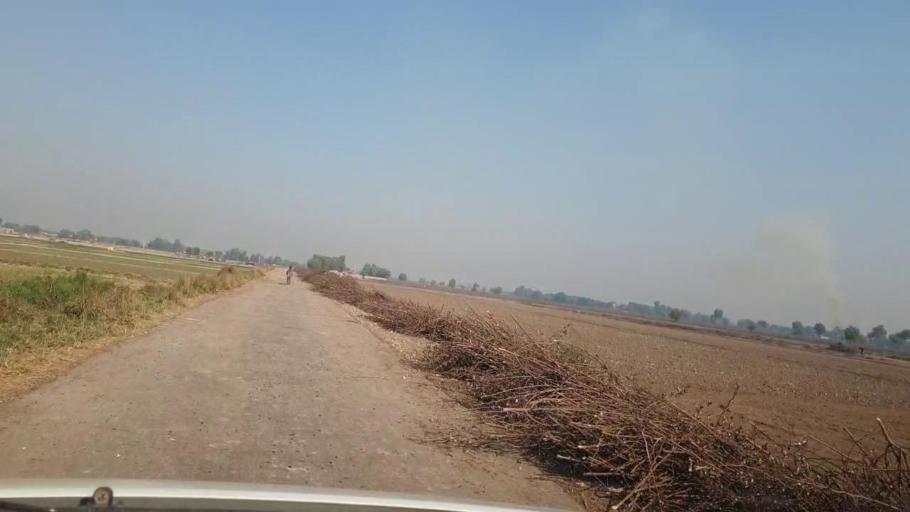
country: PK
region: Sindh
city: Bhan
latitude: 26.6118
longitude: 67.7604
